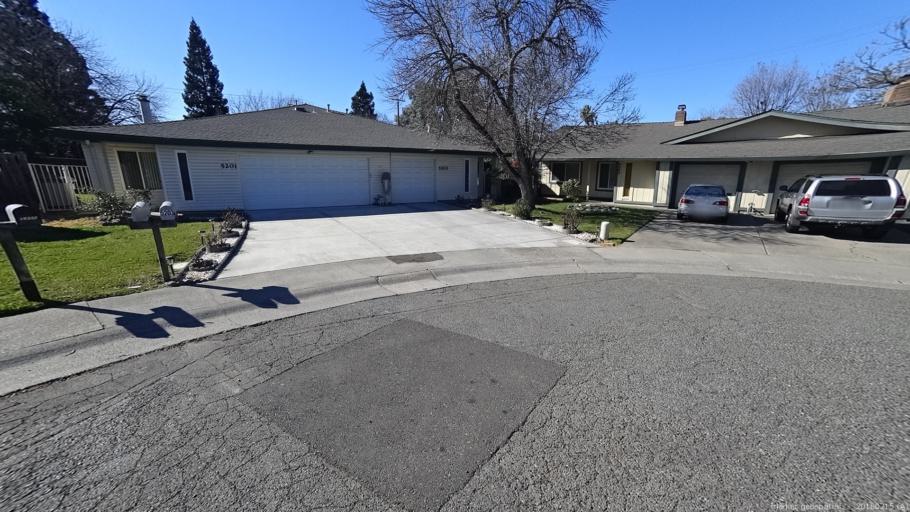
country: US
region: California
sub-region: Sacramento County
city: Foothill Farms
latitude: 38.6613
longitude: -121.3329
